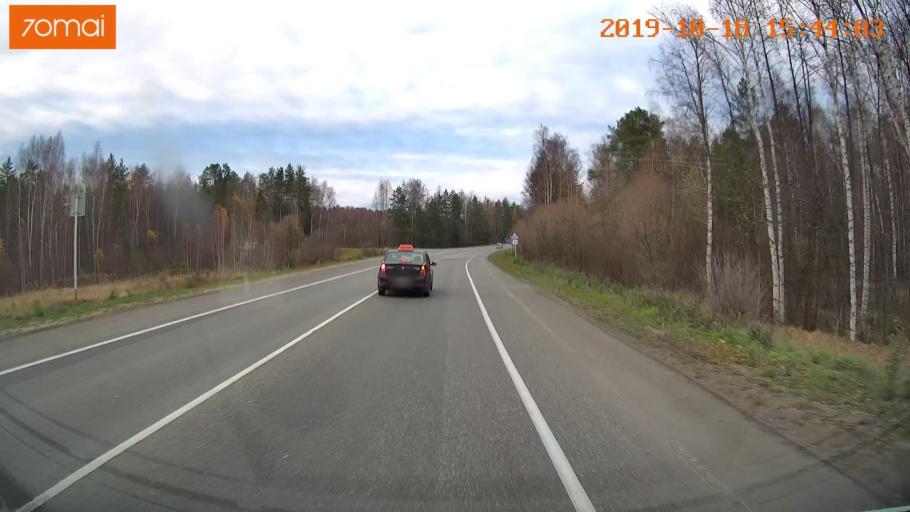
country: RU
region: Vladimir
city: Golovino
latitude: 55.9758
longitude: 40.5467
